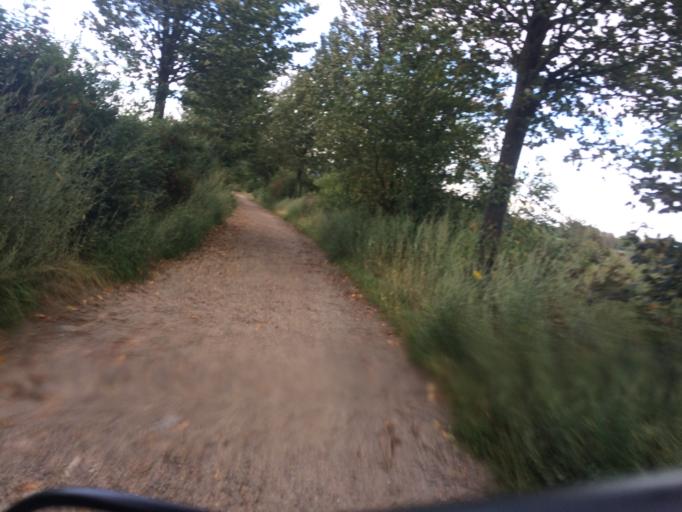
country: DE
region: Berlin
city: Stadtrandsiedlung Malchow
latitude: 52.5801
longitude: 13.4636
